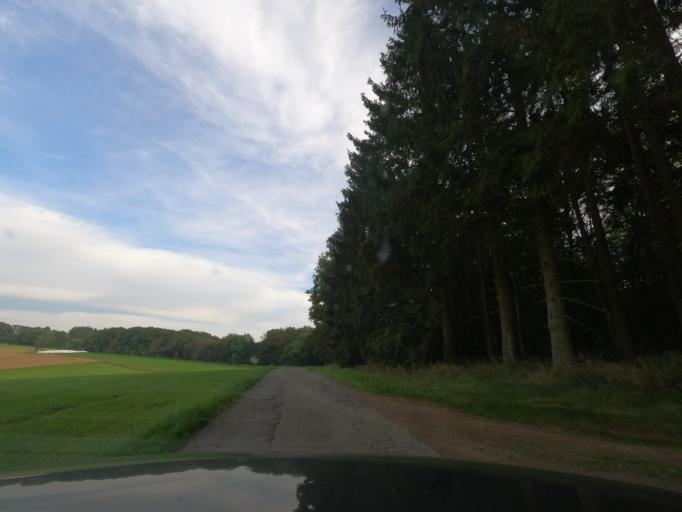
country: DE
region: North Rhine-Westphalia
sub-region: Regierungsbezirk Arnsberg
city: Herscheid
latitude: 51.2031
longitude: 7.7418
